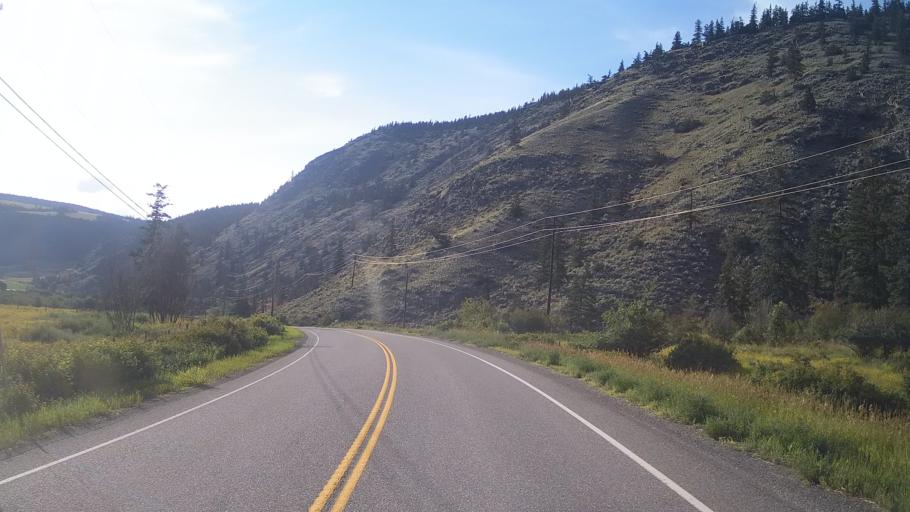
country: CA
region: British Columbia
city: Lillooet
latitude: 50.8927
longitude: -121.7618
